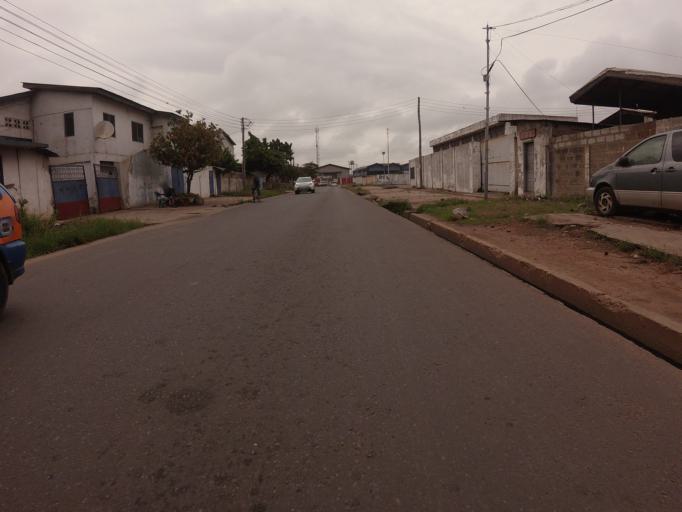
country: GH
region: Greater Accra
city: Accra
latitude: 5.5577
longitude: -0.2274
